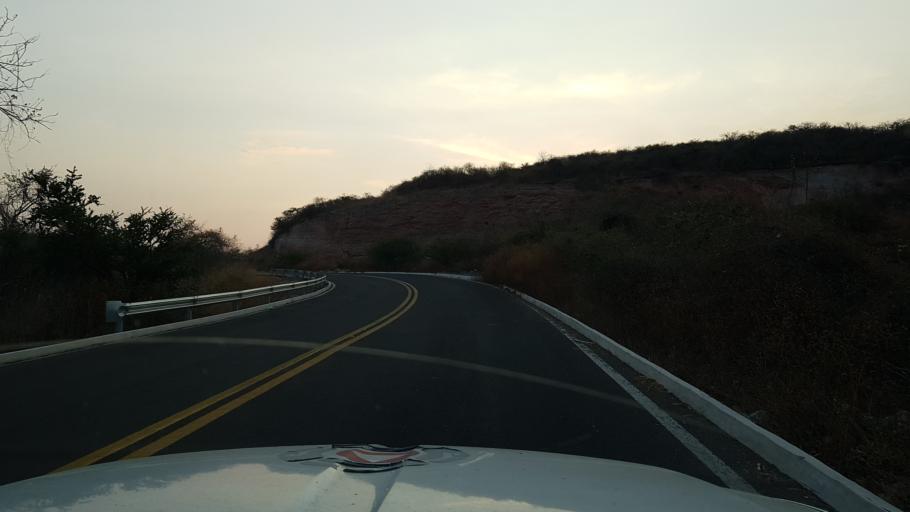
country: MX
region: Morelos
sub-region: Ayala
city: Olintepec
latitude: 18.7329
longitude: -99.0177
